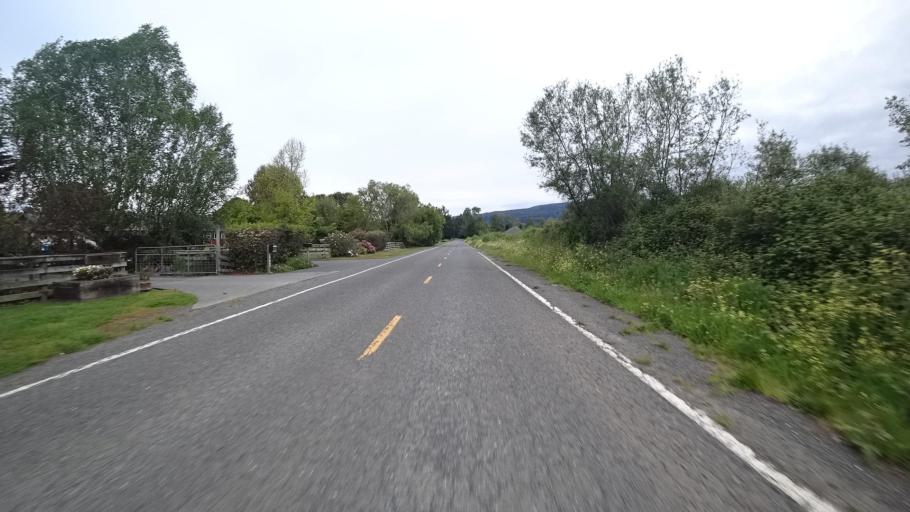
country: US
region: California
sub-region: Humboldt County
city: Blue Lake
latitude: 40.8646
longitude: -123.9957
